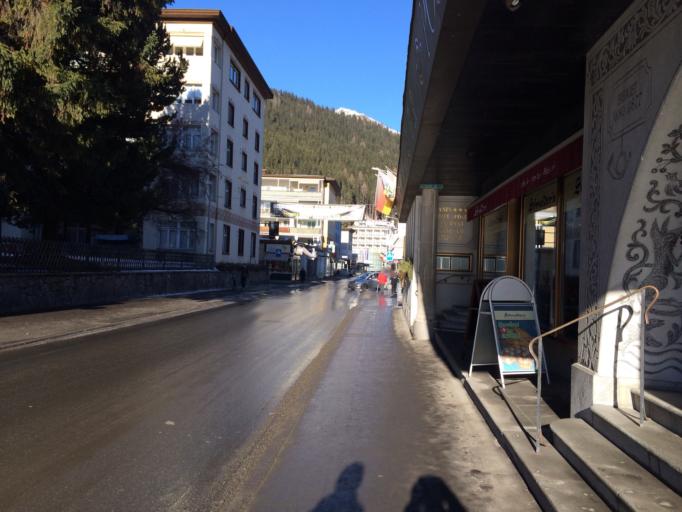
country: CH
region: Grisons
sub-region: Praettigau/Davos District
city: Davos
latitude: 46.7939
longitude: 9.8209
